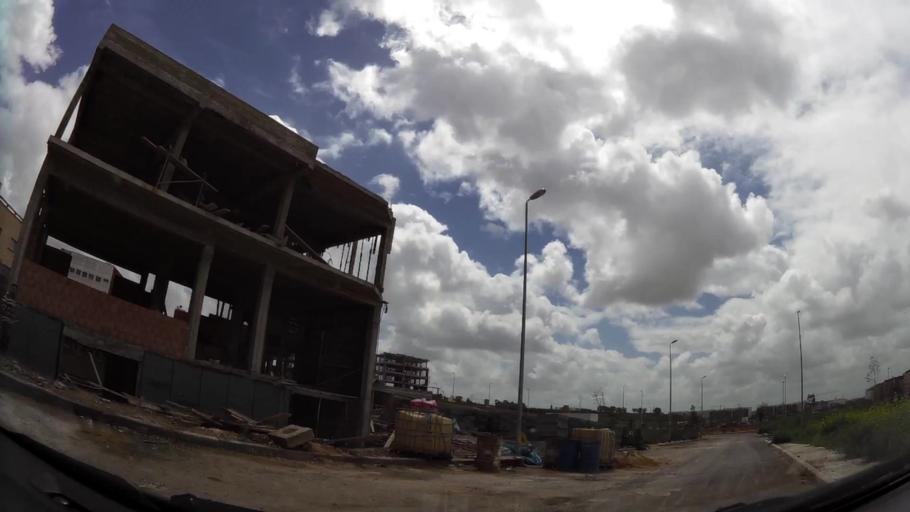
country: MA
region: Grand Casablanca
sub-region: Casablanca
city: Casablanca
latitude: 33.5297
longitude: -7.6036
